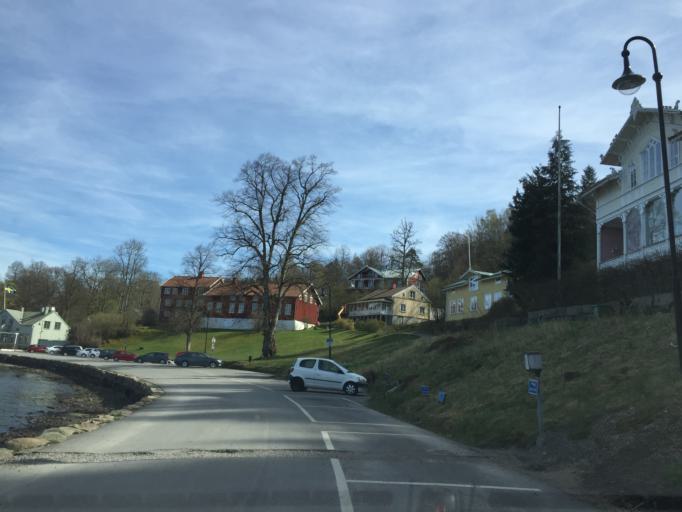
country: SE
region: Vaestra Goetaland
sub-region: Uddevalla Kommun
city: Uddevalla
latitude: 58.3301
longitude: 11.9001
